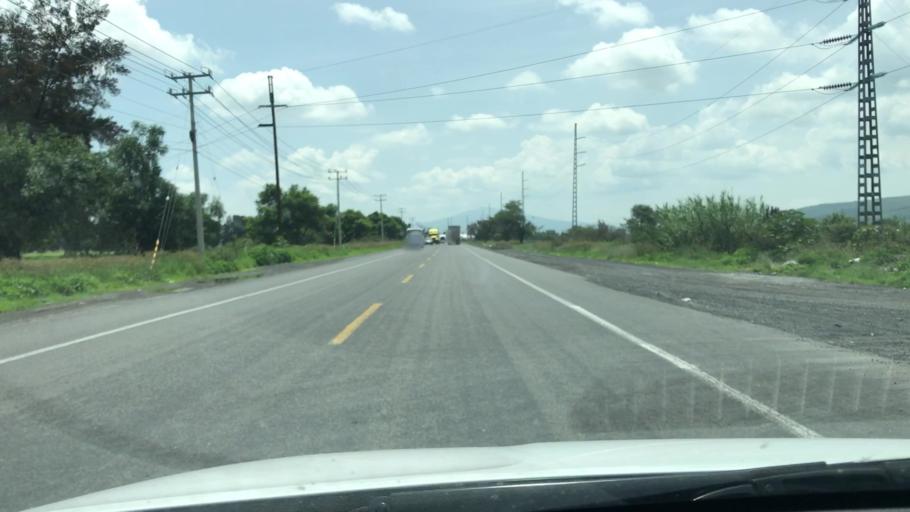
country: MX
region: Michoacan
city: Tanhuato de Guerrero
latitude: 20.2817
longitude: -102.3505
